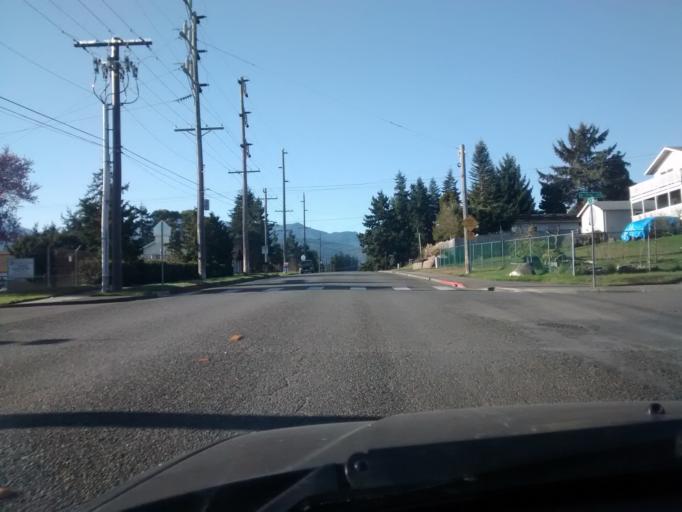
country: US
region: Washington
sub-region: Clallam County
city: Port Angeles
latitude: 48.1262
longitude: -123.4681
